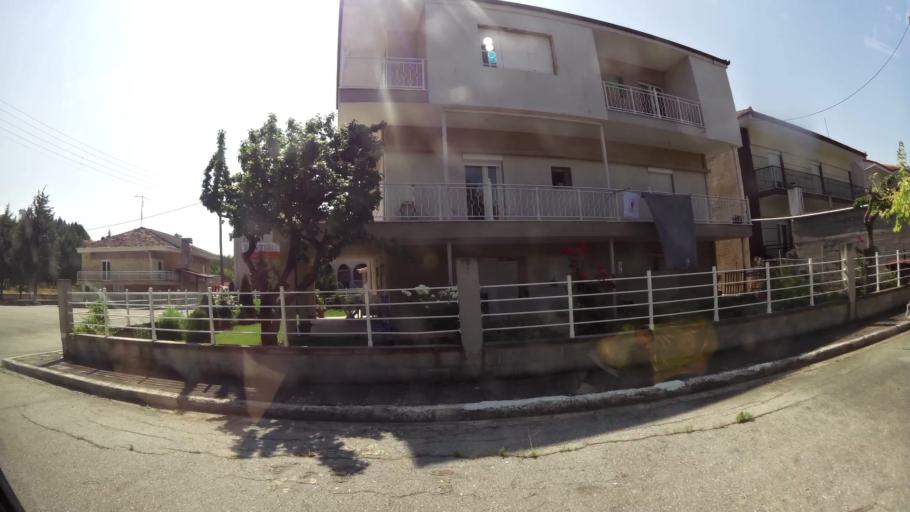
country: GR
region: West Macedonia
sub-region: Nomos Kozanis
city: Koila
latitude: 40.3379
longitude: 21.7874
